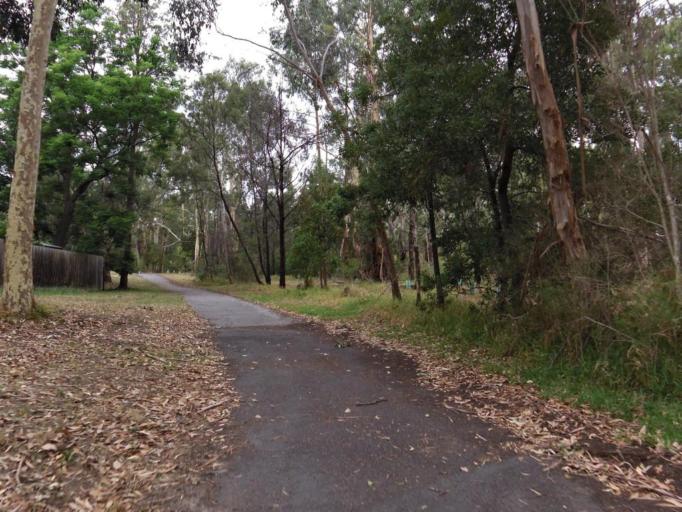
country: AU
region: Victoria
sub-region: Manningham
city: Templestowe Lower
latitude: -37.7598
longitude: 145.1250
